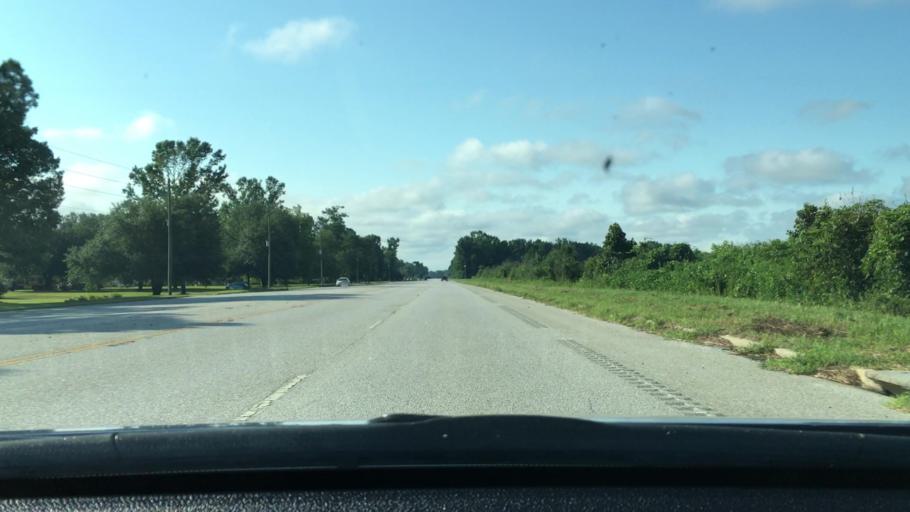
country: US
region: South Carolina
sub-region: Clarendon County
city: Manning
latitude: 33.7656
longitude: -80.2326
